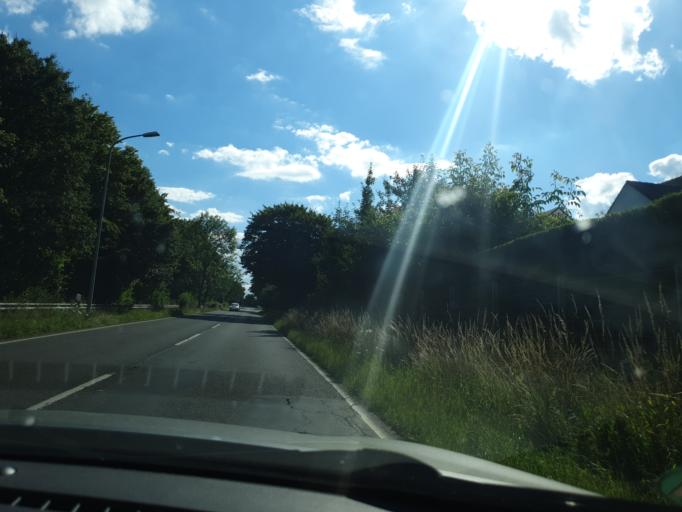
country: DE
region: North Rhine-Westphalia
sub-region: Regierungsbezirk Koln
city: Wachtberg
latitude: 50.6230
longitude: 7.1293
